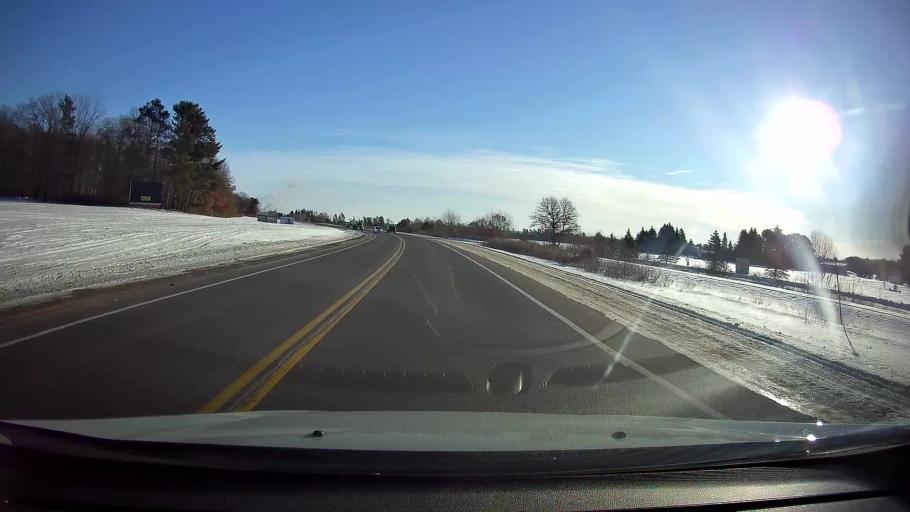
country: US
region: Wisconsin
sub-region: Sawyer County
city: Hayward
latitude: 45.9818
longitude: -91.5615
